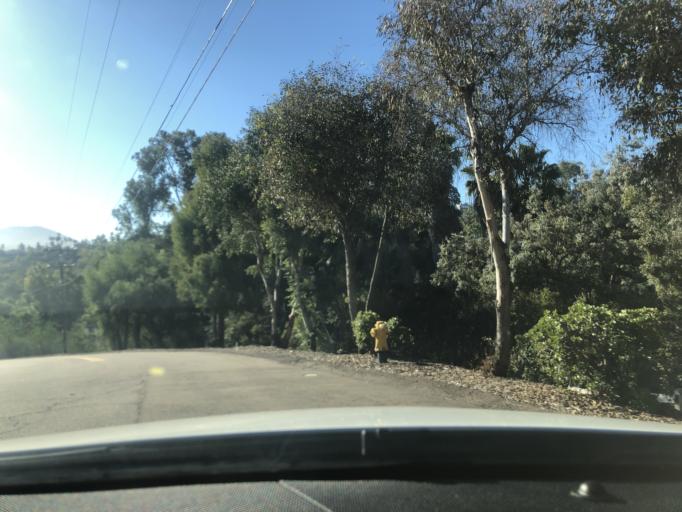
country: US
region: California
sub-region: San Diego County
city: Casa de Oro-Mount Helix
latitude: 32.7655
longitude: -116.9557
